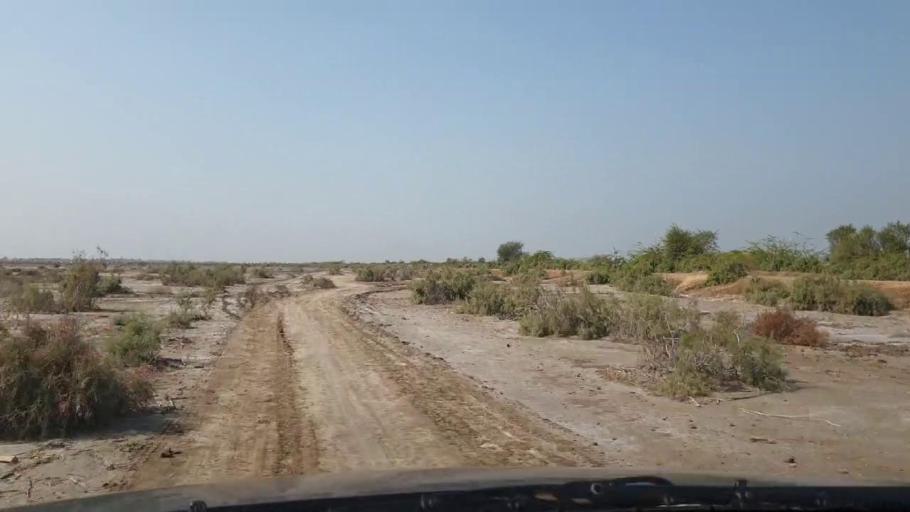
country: PK
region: Sindh
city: Jhol
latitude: 25.8893
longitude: 68.9747
